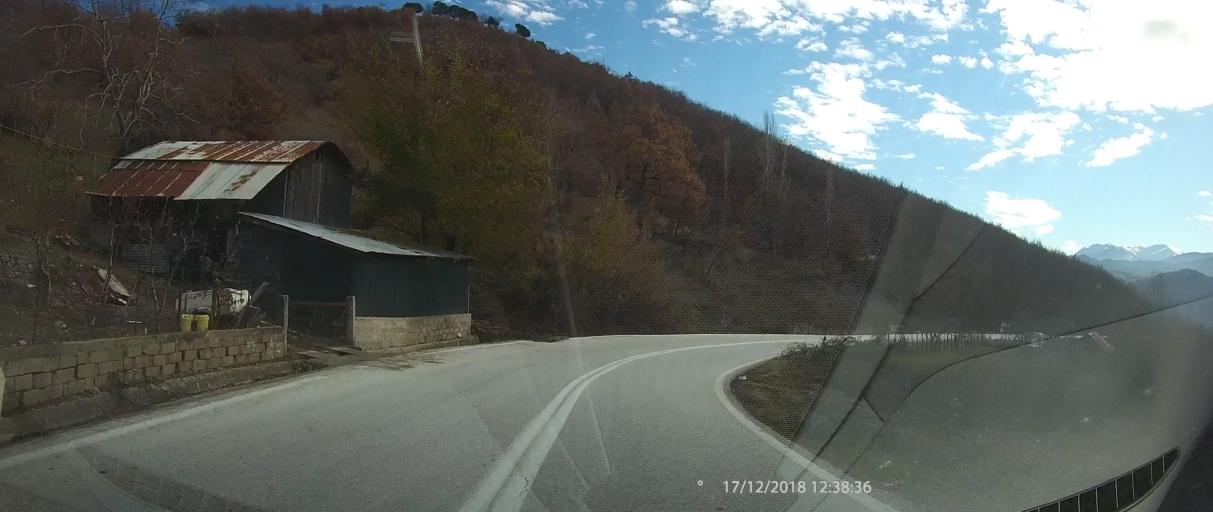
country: GR
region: Epirus
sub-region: Nomos Ioanninon
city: Metsovo
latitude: 39.8086
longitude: 21.3476
